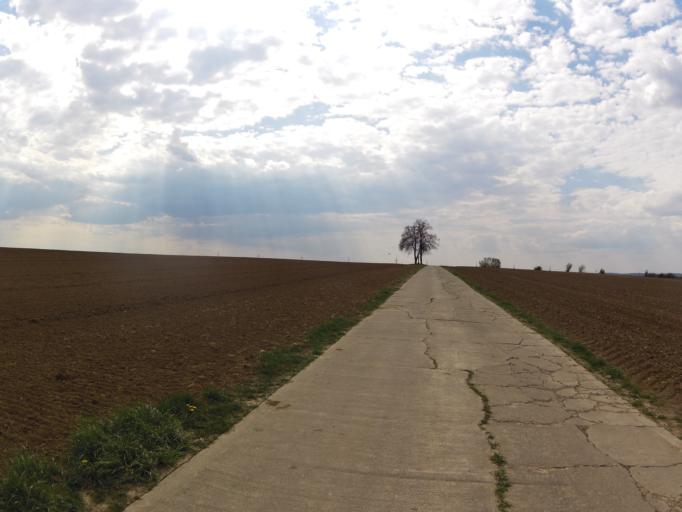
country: DE
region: Bavaria
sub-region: Regierungsbezirk Unterfranken
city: Oberpleichfeld
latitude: 49.8583
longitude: 10.0919
